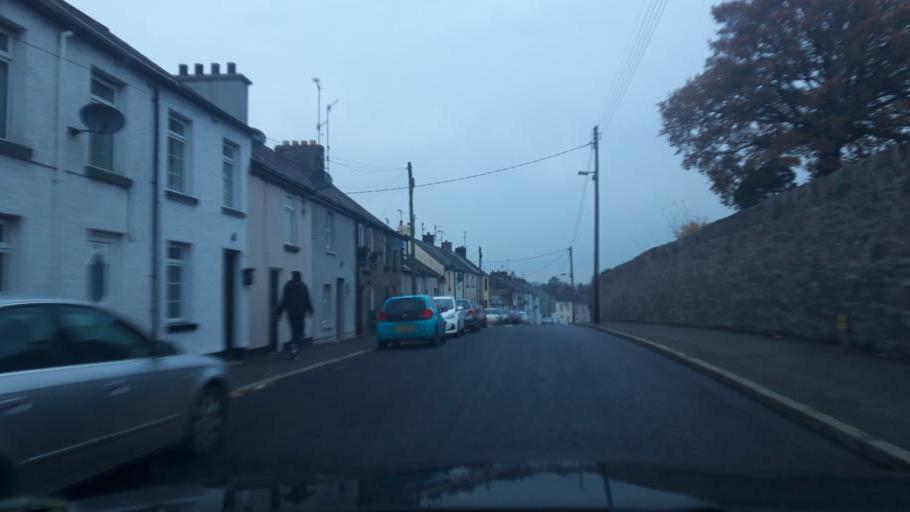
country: GB
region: Northern Ireland
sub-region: Newry and Mourne District
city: Newry
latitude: 54.1774
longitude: -6.3324
